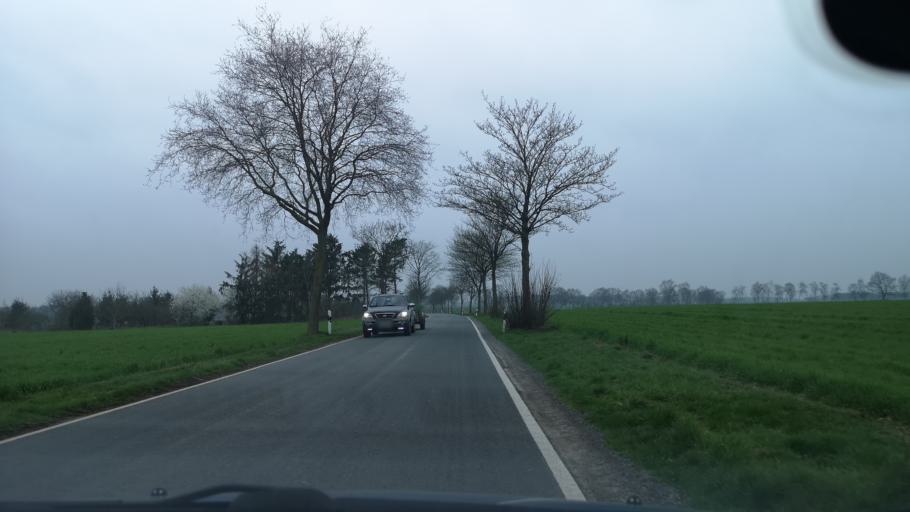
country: DE
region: Lower Saxony
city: Neustadt am Rubenberge
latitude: 52.5628
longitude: 9.4732
